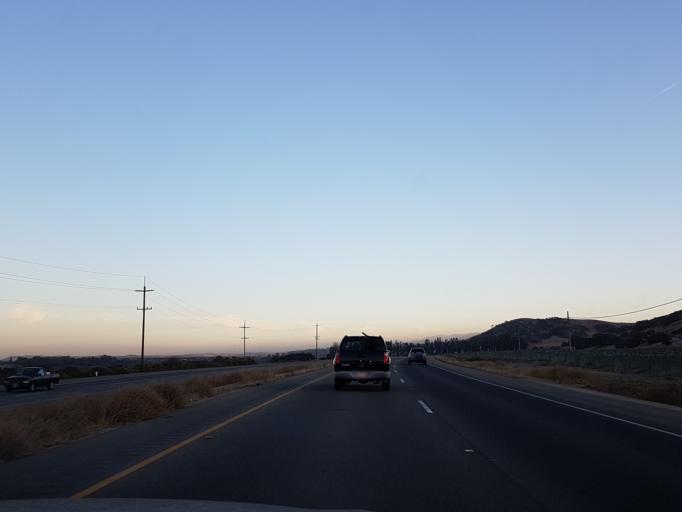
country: US
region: California
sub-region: Monterey County
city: King City
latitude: 36.2222
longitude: -121.1693
